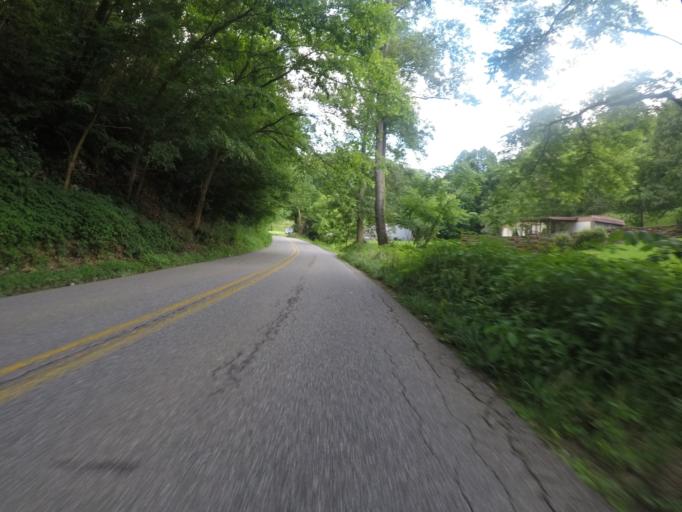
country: US
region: West Virginia
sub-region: Cabell County
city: Pea Ridge
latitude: 38.3957
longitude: -82.3624
